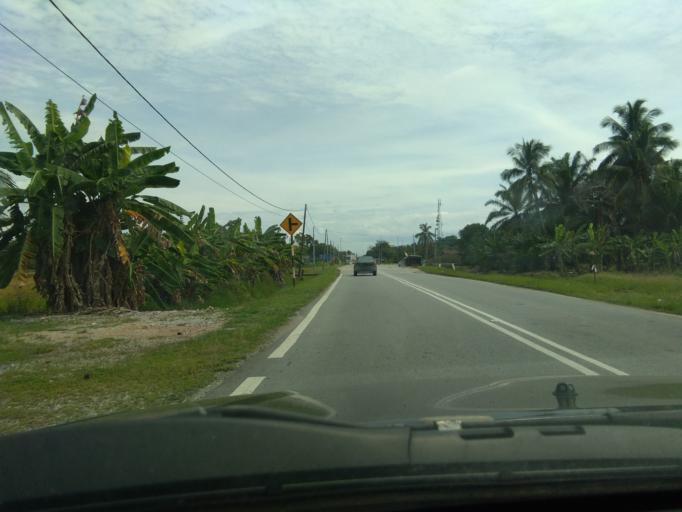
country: MY
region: Perak
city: Bagan Serai
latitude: 5.0588
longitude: 100.5939
